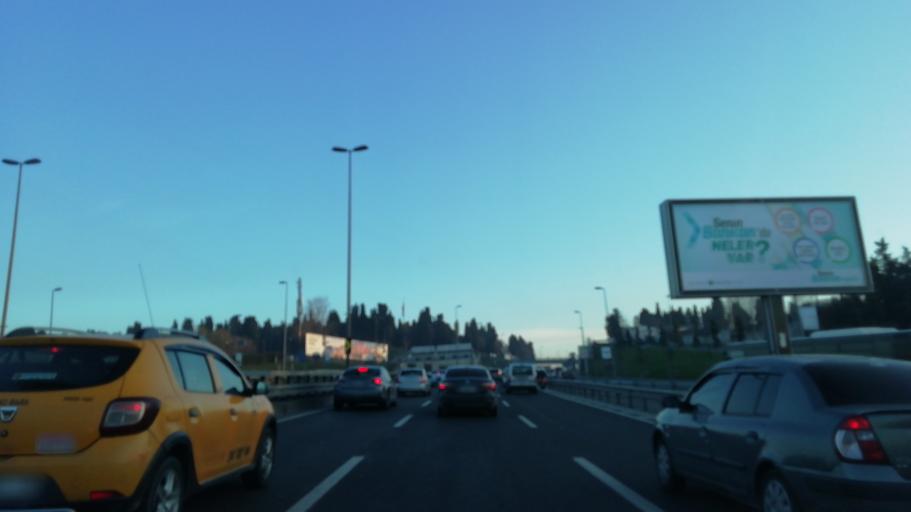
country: TR
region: Istanbul
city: Istanbul
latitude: 41.0309
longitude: 28.9257
